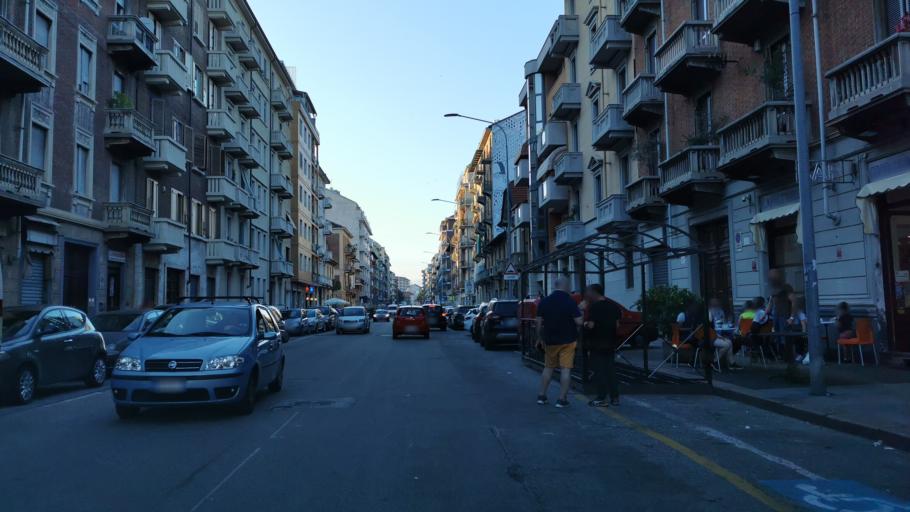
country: IT
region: Piedmont
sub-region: Provincia di Torino
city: Turin
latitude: 45.0952
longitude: 7.6938
